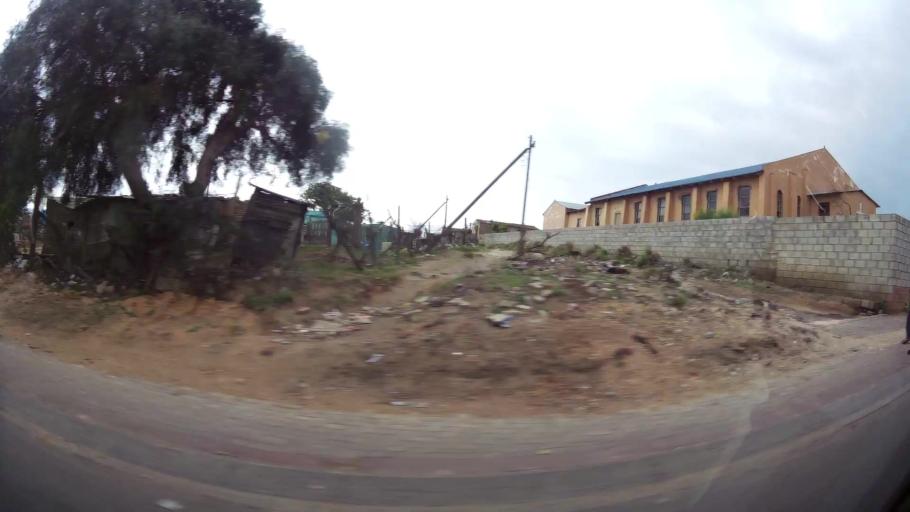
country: ZA
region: Eastern Cape
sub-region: Nelson Mandela Bay Metropolitan Municipality
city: Port Elizabeth
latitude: -33.8910
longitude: 25.5889
